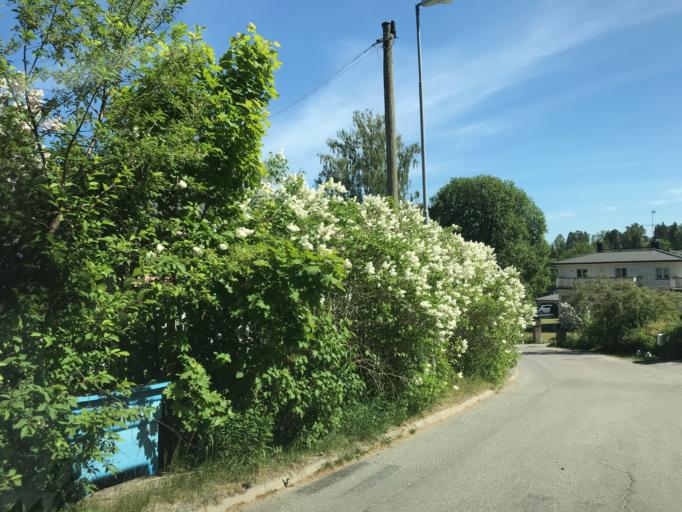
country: SE
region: Stockholm
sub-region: Sollentuna Kommun
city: Sollentuna
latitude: 59.4208
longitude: 17.9777
